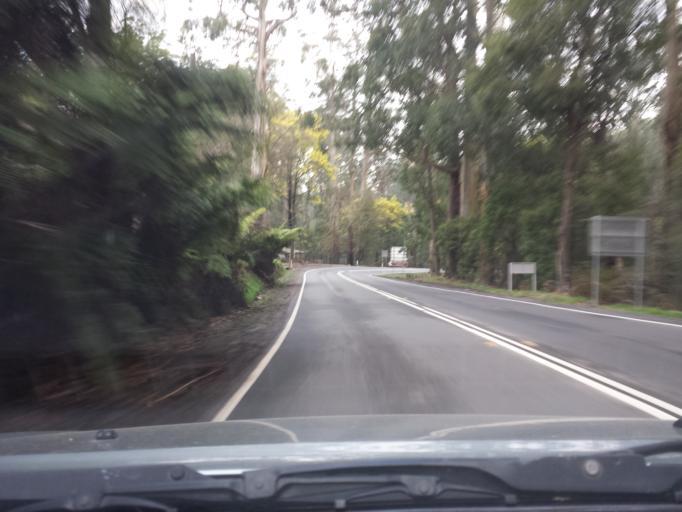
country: AU
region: Victoria
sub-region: Yarra Ranges
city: Kallista
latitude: -37.8854
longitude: 145.3695
